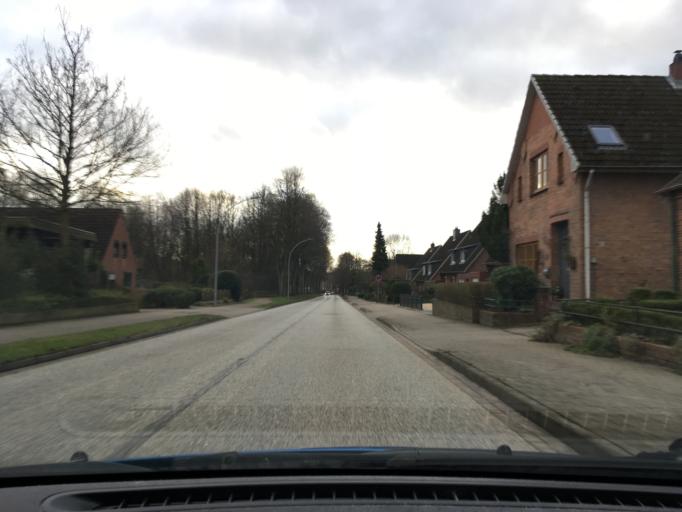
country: DE
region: Schleswig-Holstein
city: Ottenbuttel
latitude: 53.9494
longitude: 9.4944
